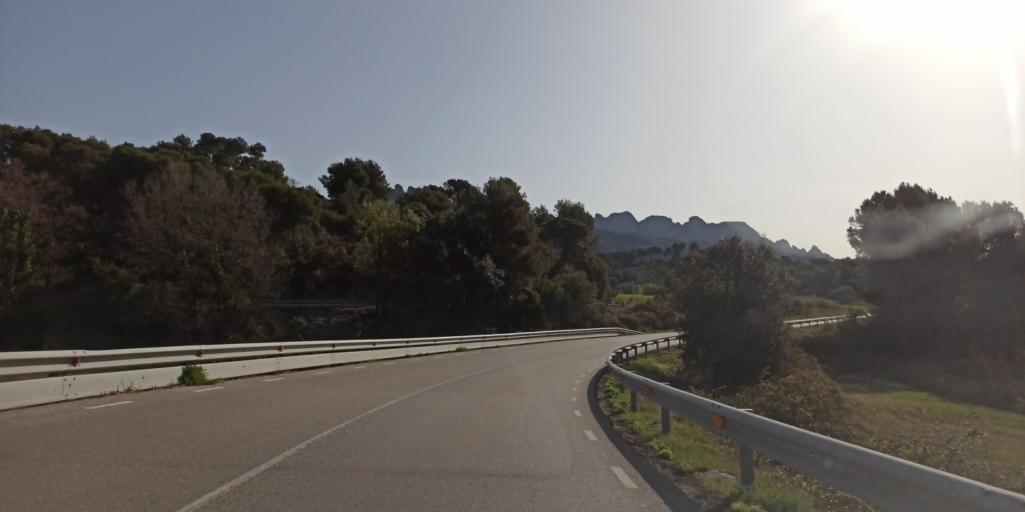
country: ES
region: Catalonia
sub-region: Provincia de Barcelona
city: Castelloli
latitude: 41.6014
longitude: 1.7594
